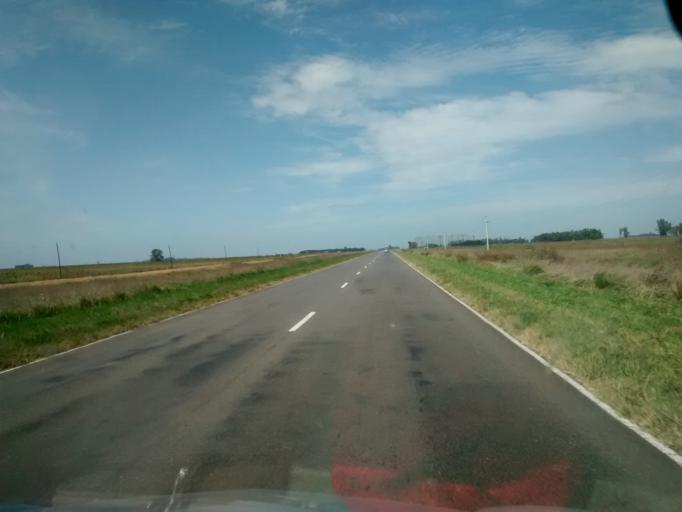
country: AR
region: Buenos Aires
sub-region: Partido de Ayacucho
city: Ayacucho
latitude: -36.8879
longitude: -58.5360
